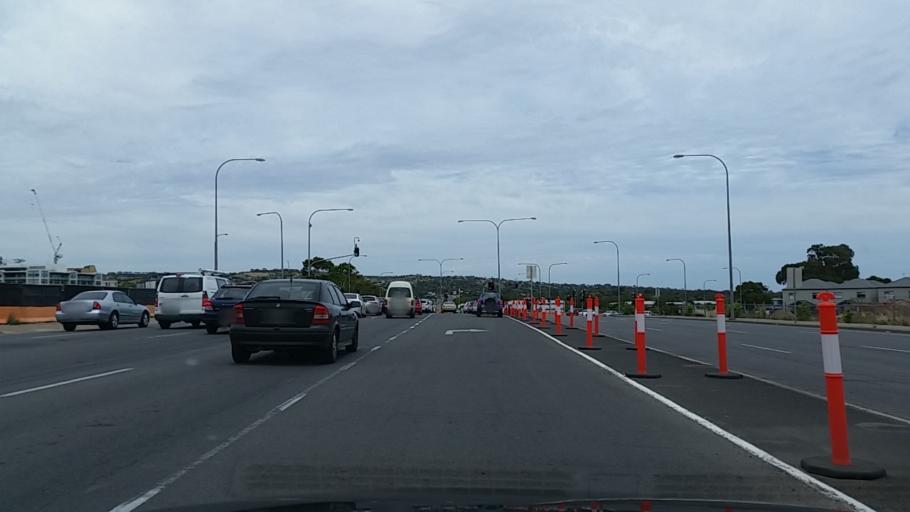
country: AU
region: South Australia
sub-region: Marion
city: Marion
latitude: -35.0157
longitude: 138.5707
